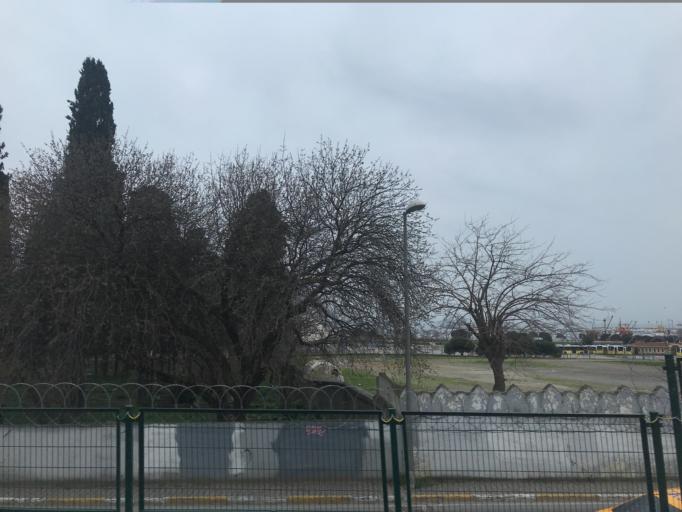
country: TR
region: Istanbul
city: Pendik
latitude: 40.8753
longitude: 29.2461
